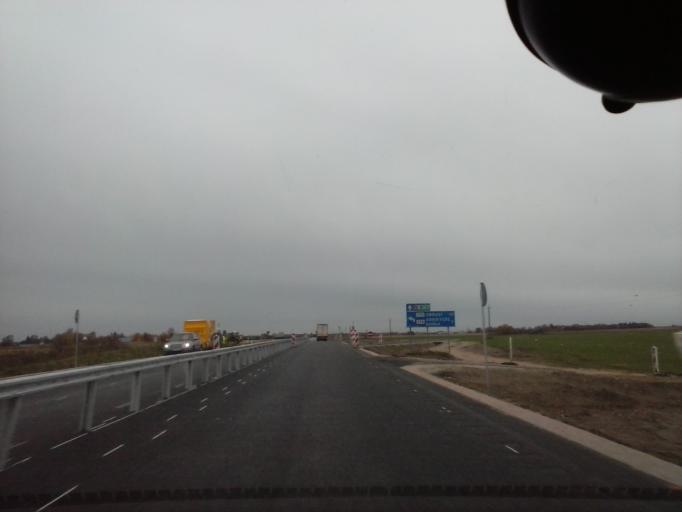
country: EE
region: Jogevamaa
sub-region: Poltsamaa linn
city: Poltsamaa
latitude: 58.6437
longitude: 26.0576
